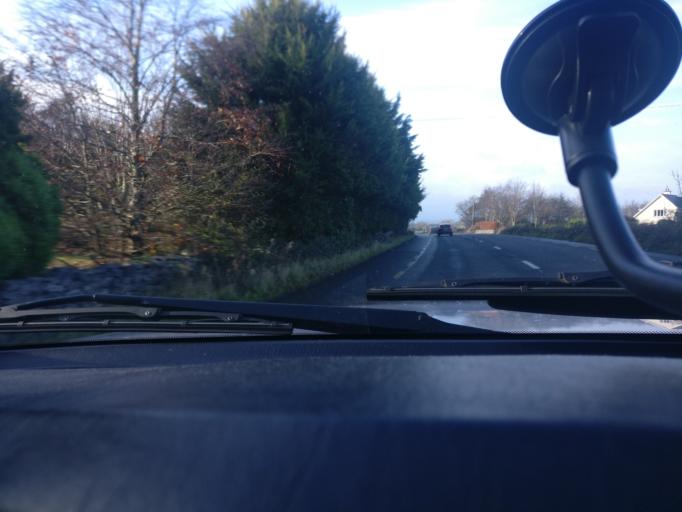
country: IE
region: Connaught
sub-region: County Galway
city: Oranmore
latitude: 53.2719
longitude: -8.8408
